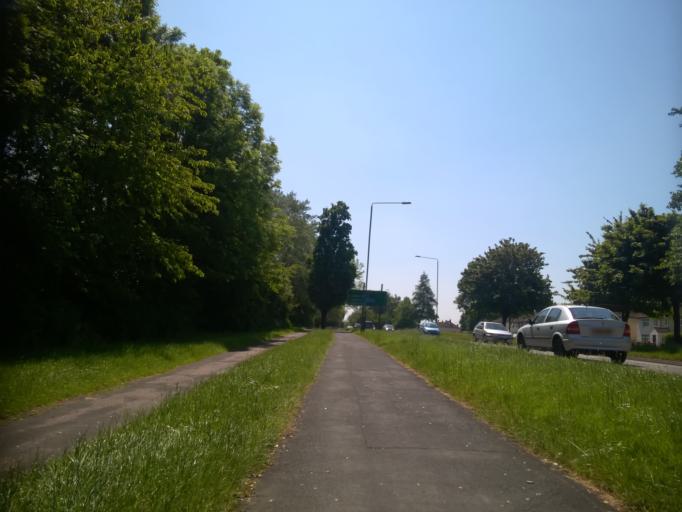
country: GB
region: England
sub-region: Leicestershire
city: Glenfield
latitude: 52.6410
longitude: -1.1846
